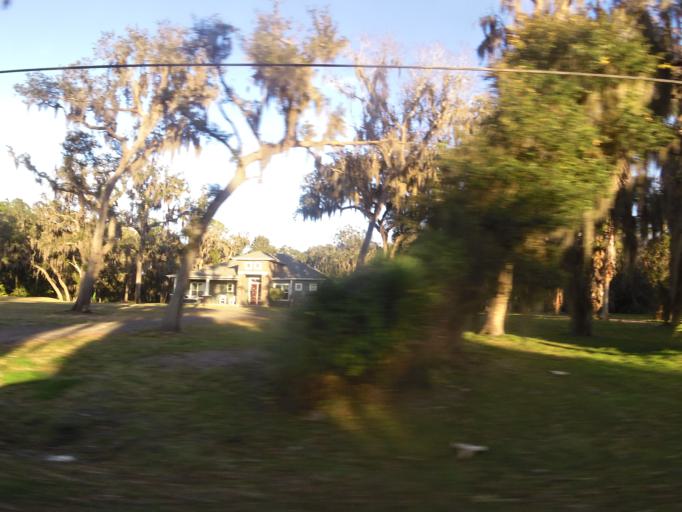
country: US
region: Florida
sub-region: Putnam County
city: East Palatka
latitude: 29.8035
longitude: -81.5502
